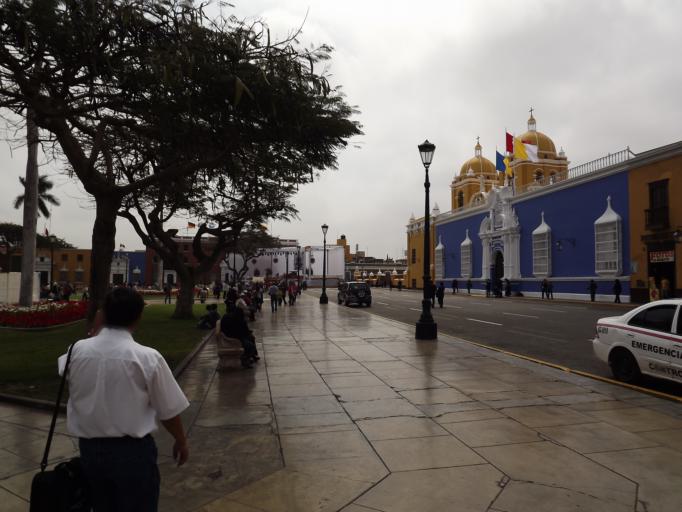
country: PE
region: La Libertad
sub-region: Provincia de Trujillo
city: Trujillo
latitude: -8.1117
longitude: -79.0281
